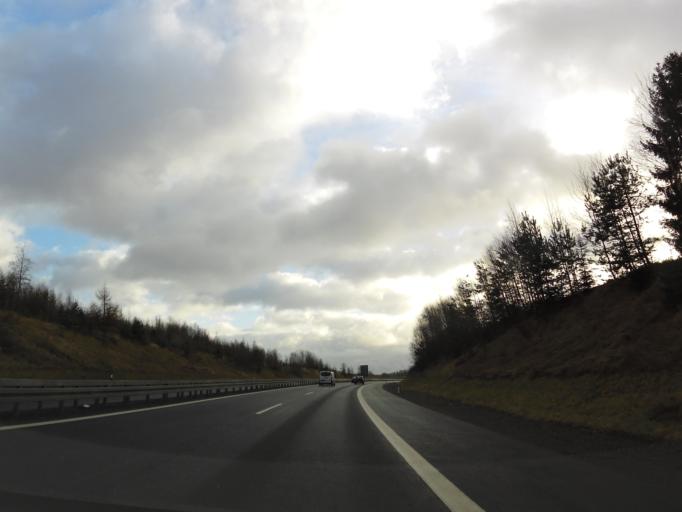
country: DE
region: Bavaria
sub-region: Upper Franconia
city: Thierstein
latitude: 50.0970
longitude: 12.0994
